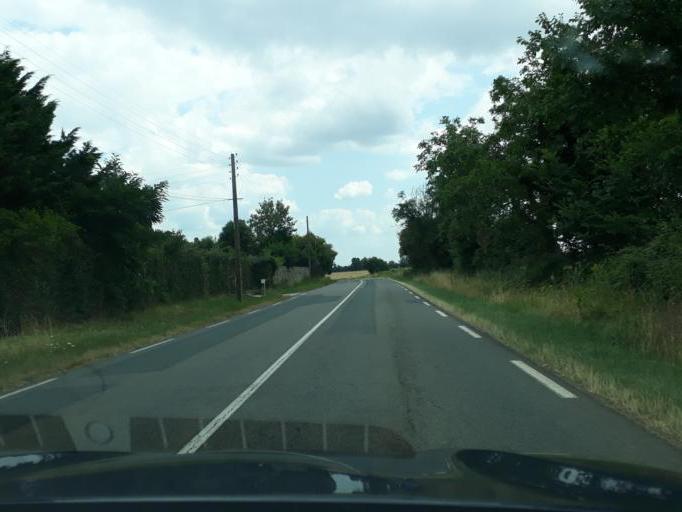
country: FR
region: Centre
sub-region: Departement du Cher
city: Avord
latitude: 47.0217
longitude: 2.6827
